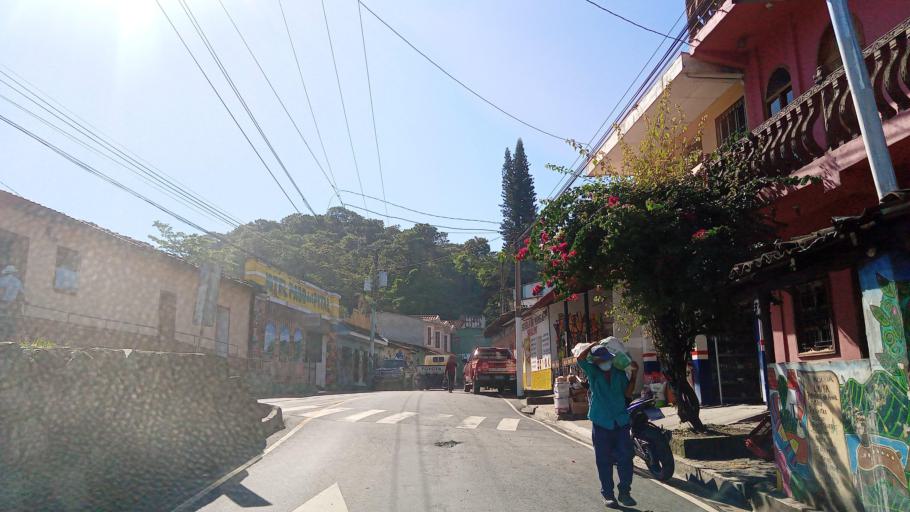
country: HN
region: Ocotepeque
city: Antigua Ocotepeque
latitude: 14.3156
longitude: -89.1688
